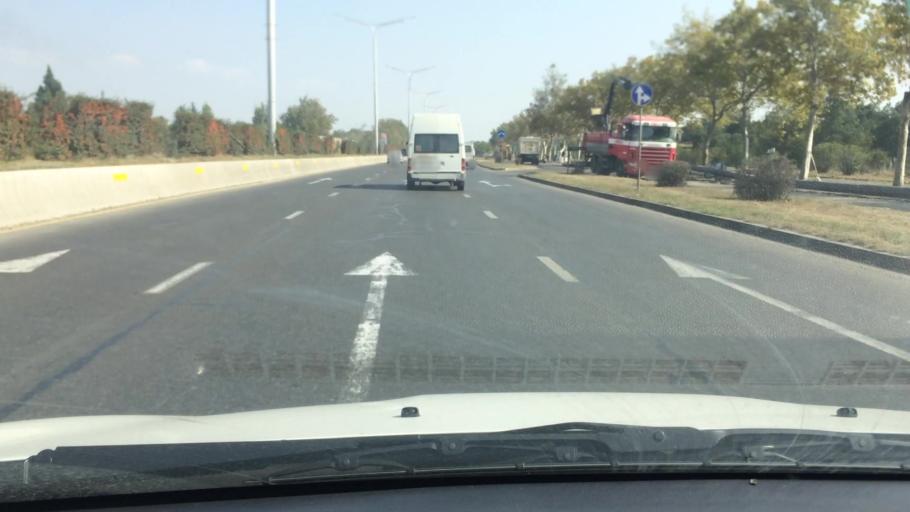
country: GE
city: Didi Lilo
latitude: 41.6890
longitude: 44.9120
